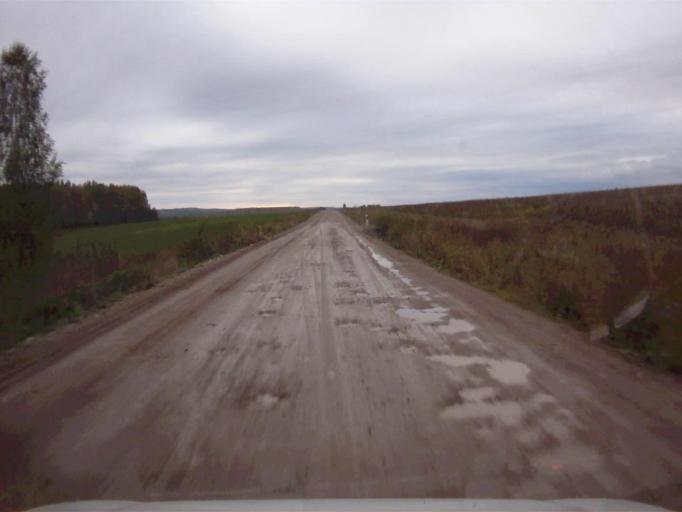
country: RU
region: Sverdlovsk
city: Mikhaylovsk
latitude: 56.1784
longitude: 59.2020
